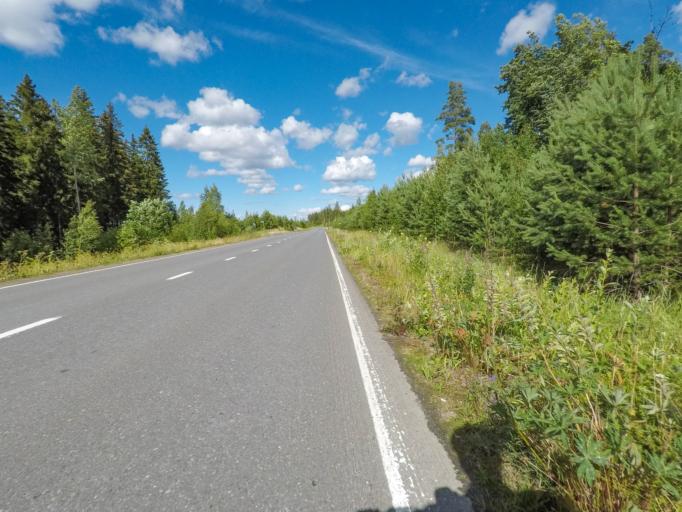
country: FI
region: South Karelia
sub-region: Lappeenranta
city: Joutseno
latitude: 61.0937
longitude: 28.3531
